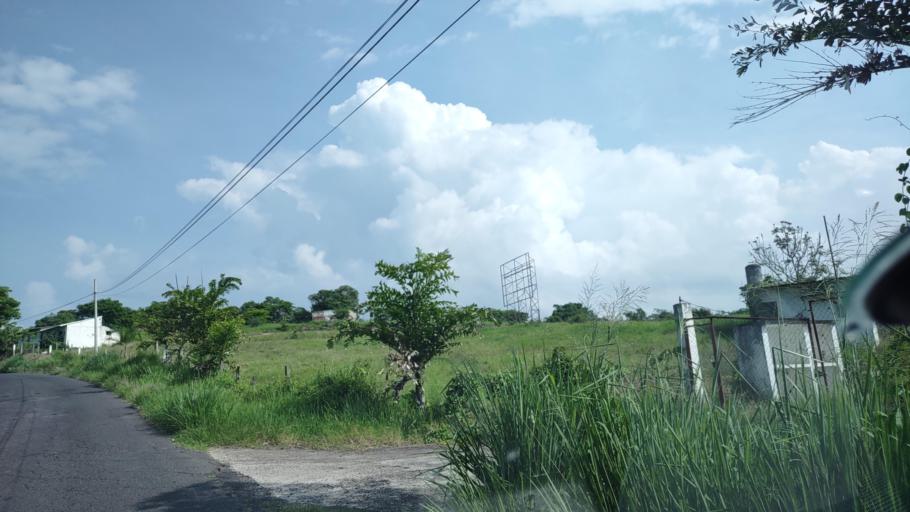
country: MX
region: Veracruz
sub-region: Coatepec
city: Bella Esperanza
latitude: 19.4555
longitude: -96.8337
